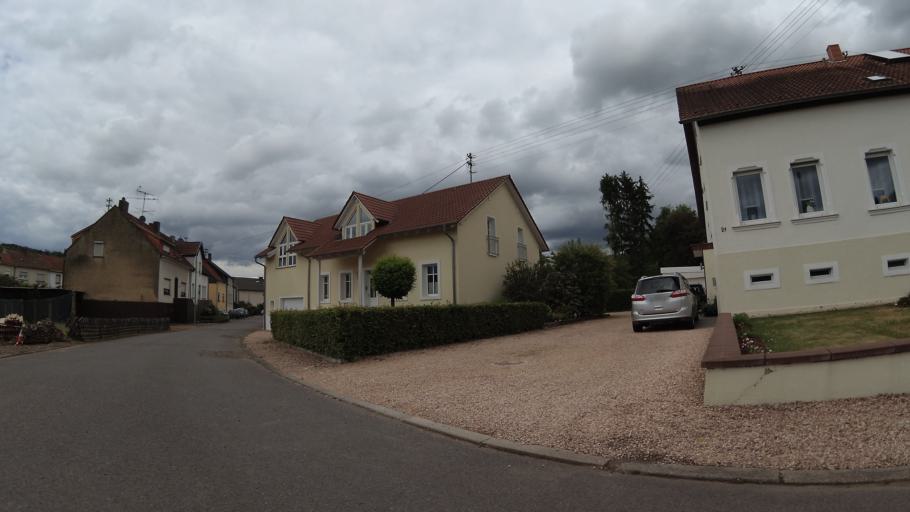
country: DE
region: Saarland
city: Saarwellingen
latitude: 49.3887
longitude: 6.8341
